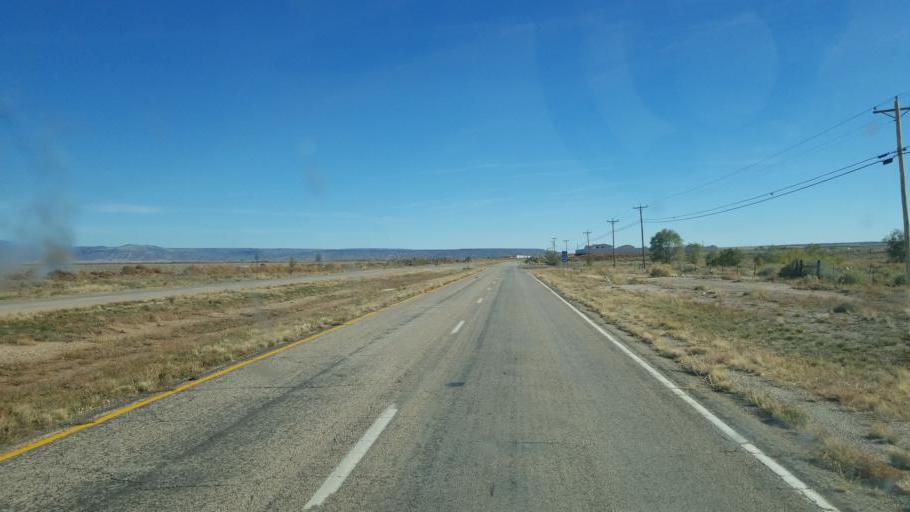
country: US
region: New Mexico
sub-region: Cibola County
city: Milan
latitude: 35.2659
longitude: -107.9741
